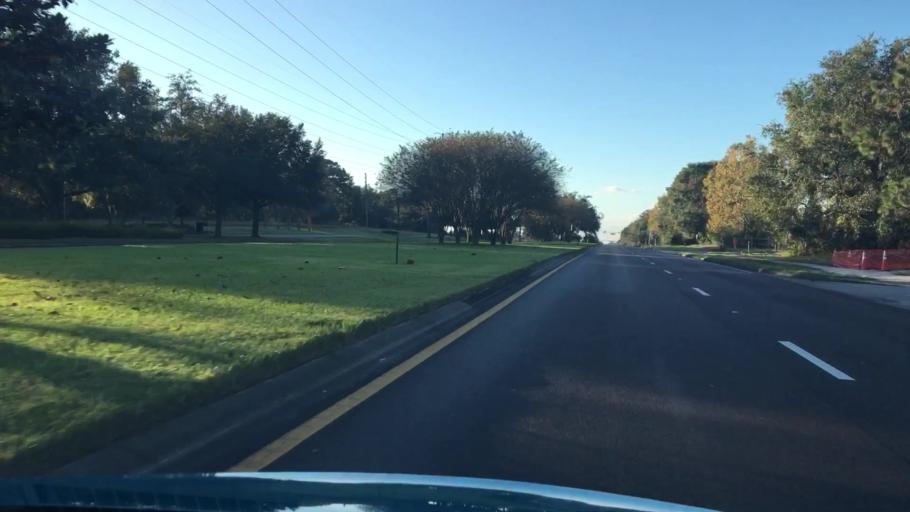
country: US
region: Florida
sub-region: Seminole County
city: Heathrow
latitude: 28.7704
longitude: -81.3472
